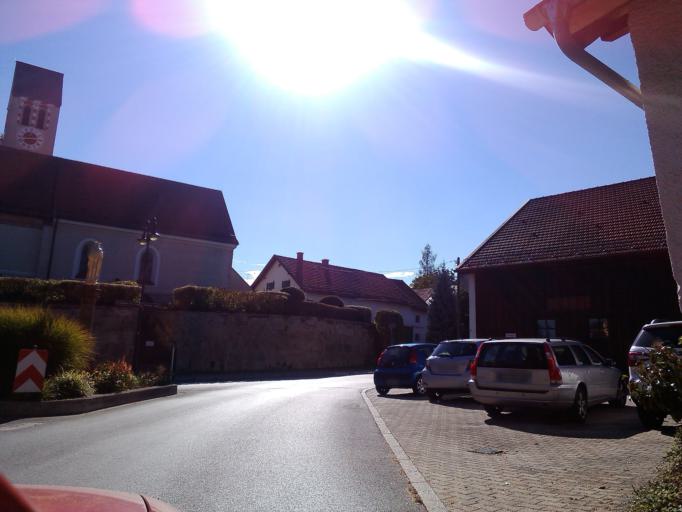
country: DE
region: Bavaria
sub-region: Upper Bavaria
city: Gauting
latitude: 48.0576
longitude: 11.4028
